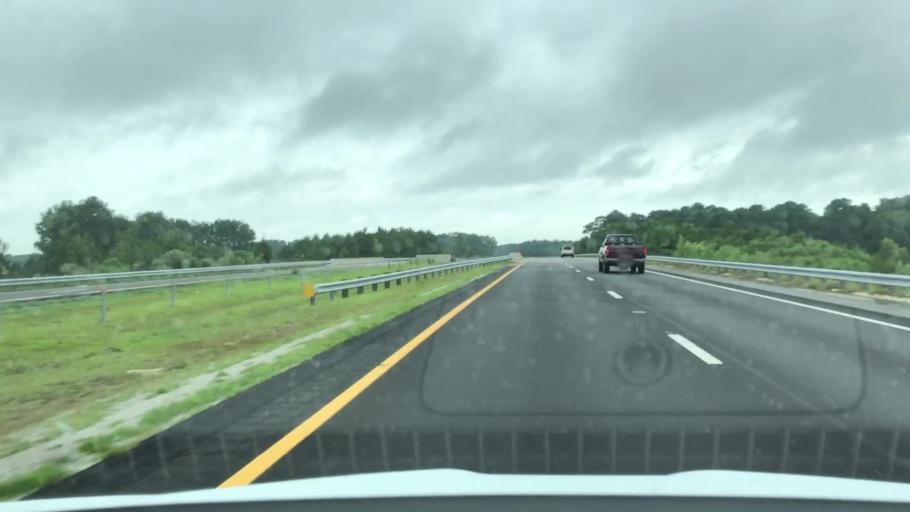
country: US
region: North Carolina
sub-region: Wayne County
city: Fremont
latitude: 35.4682
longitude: -77.9864
